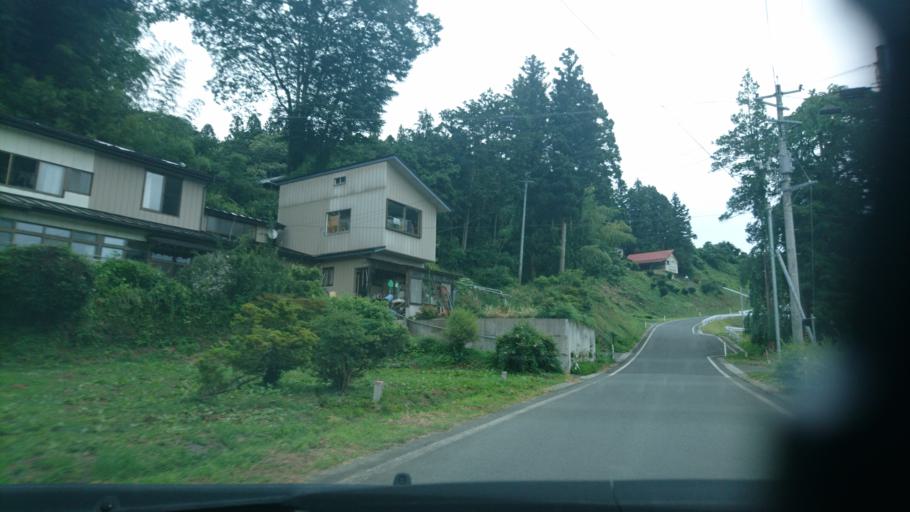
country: JP
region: Iwate
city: Ichinoseki
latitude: 38.9016
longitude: 141.2902
